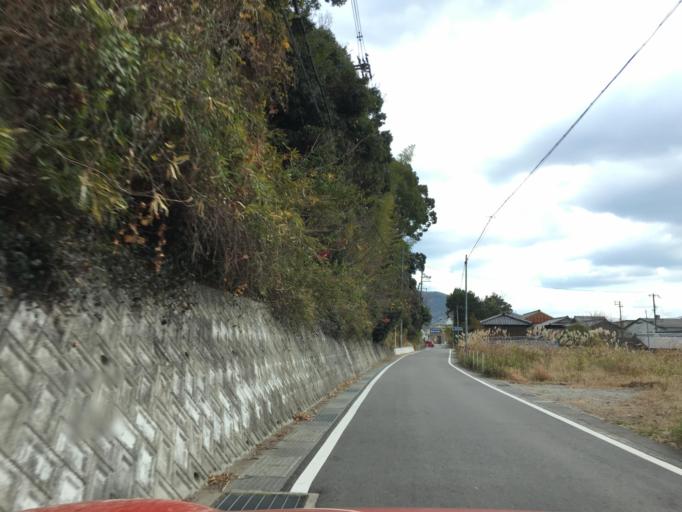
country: JP
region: Wakayama
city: Iwade
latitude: 34.1642
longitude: 135.2899
